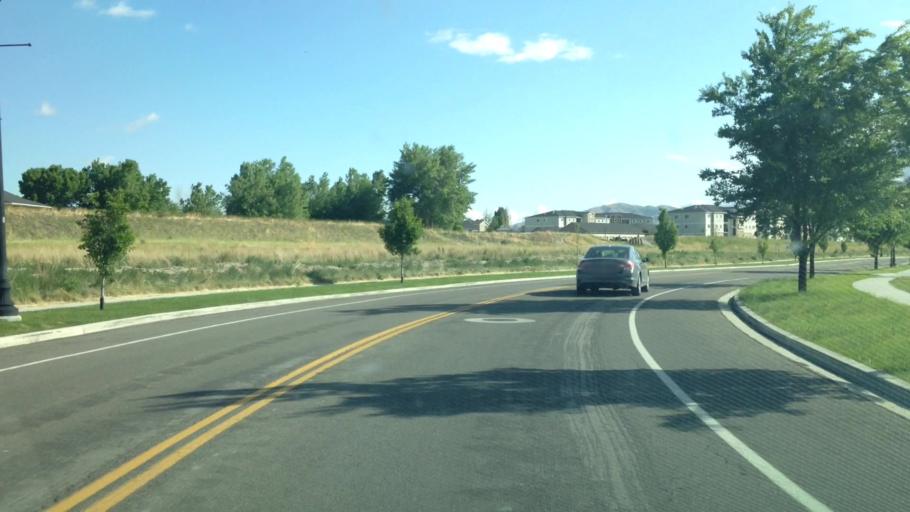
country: US
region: Utah
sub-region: Utah County
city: Saratoga Springs
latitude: 40.3929
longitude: -111.9237
